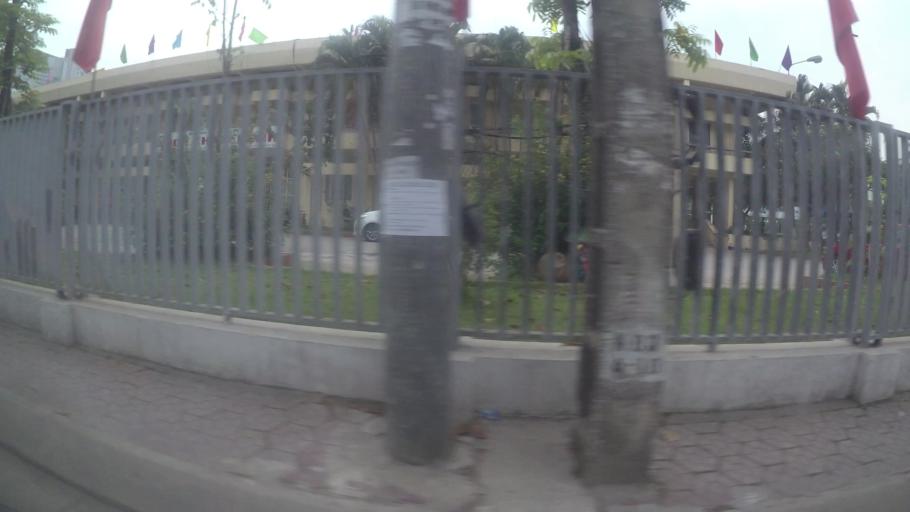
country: VN
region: Ha Noi
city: Cau Dien
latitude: 21.0336
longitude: 105.7788
